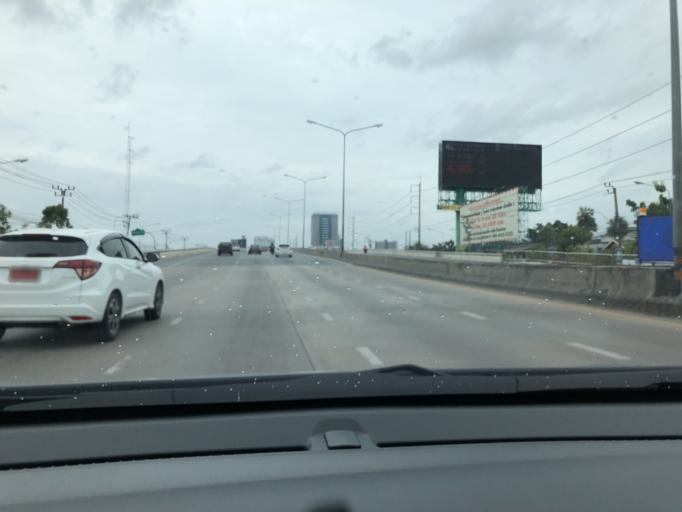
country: TH
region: Bangkok
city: Suan Luang
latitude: 13.7142
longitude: 100.6434
